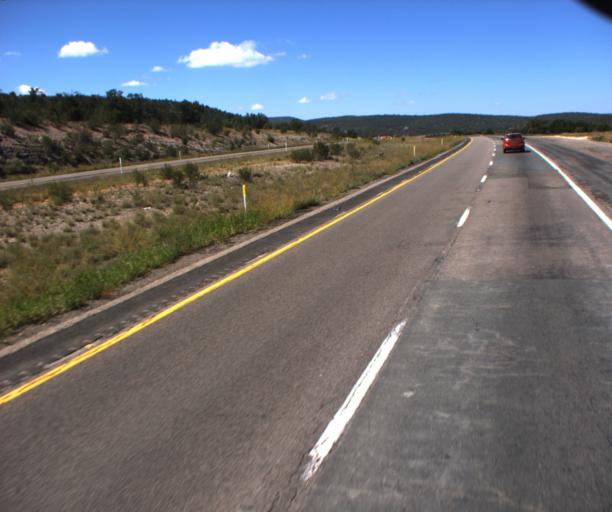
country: US
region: Arizona
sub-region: Mohave County
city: Peach Springs
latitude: 35.3007
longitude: -113.0204
